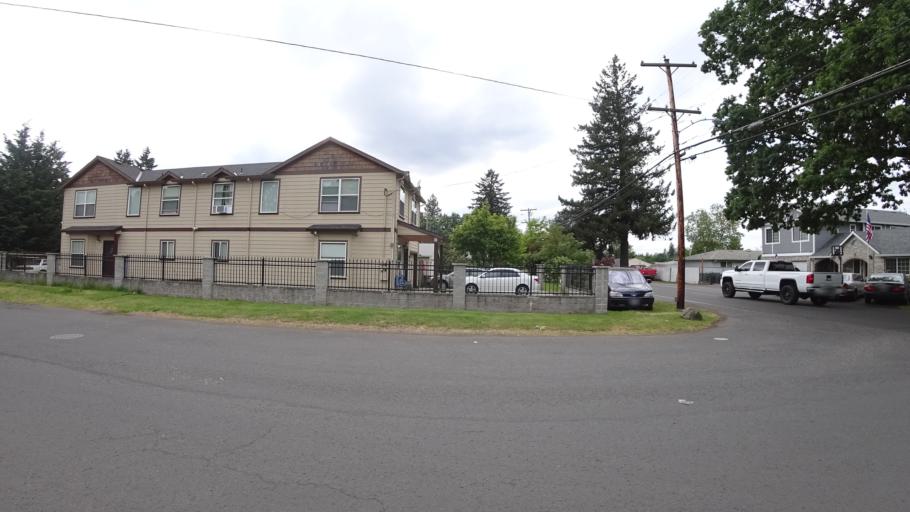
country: US
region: Oregon
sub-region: Multnomah County
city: Gresham
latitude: 45.5135
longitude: -122.4886
